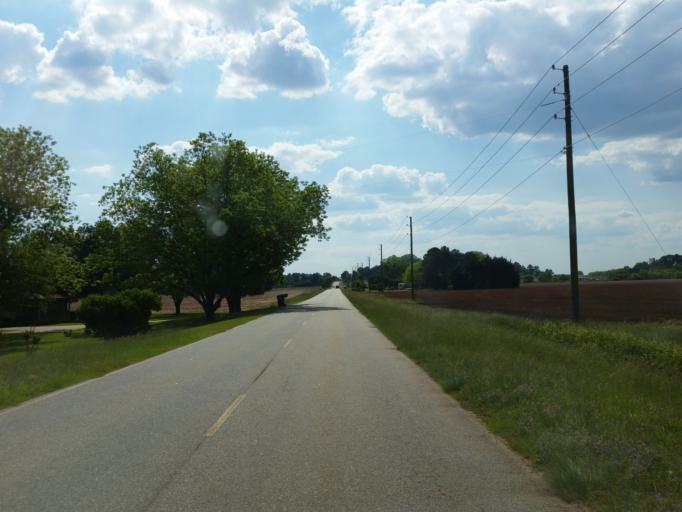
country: US
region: Georgia
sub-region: Houston County
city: Centerville
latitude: 32.5781
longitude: -83.7332
